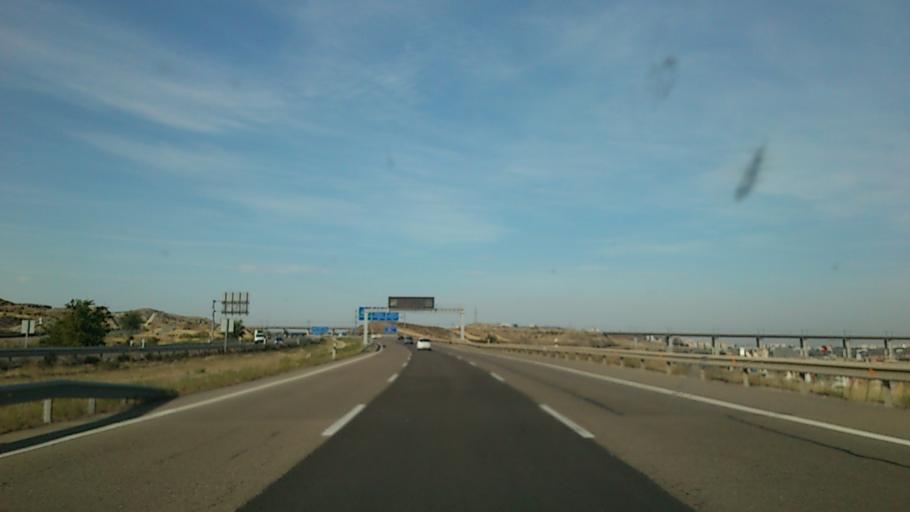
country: ES
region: Aragon
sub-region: Provincia de Zaragoza
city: Cuarte de Huerva
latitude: 41.6004
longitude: -0.9377
